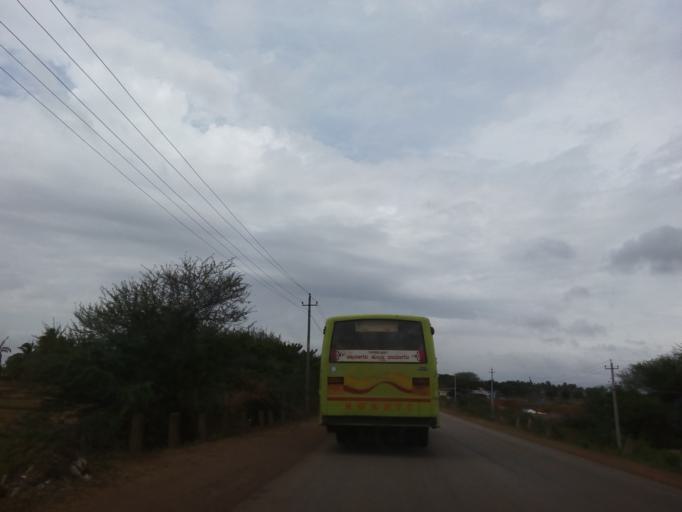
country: IN
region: Karnataka
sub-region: Davanagere
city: Harihar
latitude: 14.5101
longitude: 75.7826
